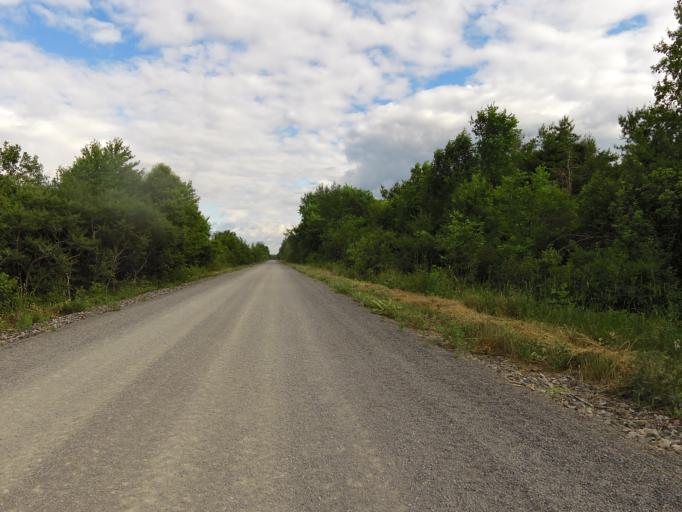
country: CA
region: Ontario
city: Arnprior
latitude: 45.2927
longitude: -76.2576
